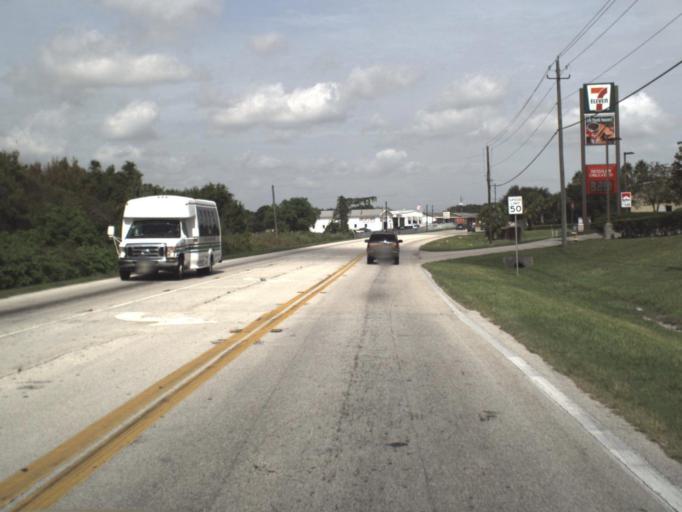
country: US
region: Florida
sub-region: Polk County
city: Jan-Phyl Village
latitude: 28.0261
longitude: -81.7764
